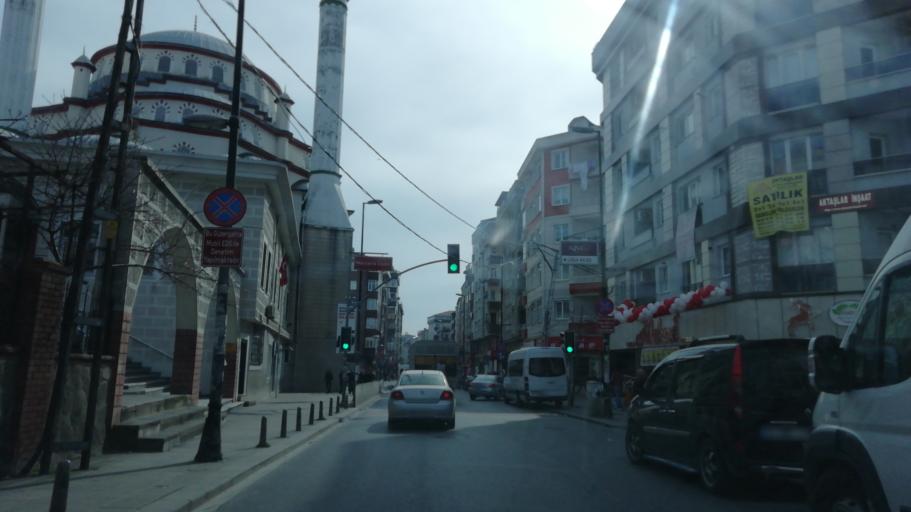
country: TR
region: Istanbul
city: Bahcelievler
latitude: 41.0100
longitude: 28.8390
